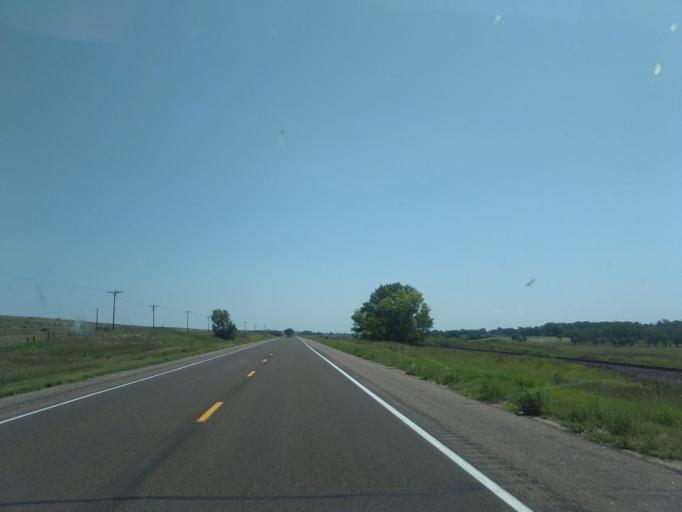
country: US
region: Nebraska
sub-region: Dundy County
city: Benkelman
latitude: 40.1229
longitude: -101.3730
